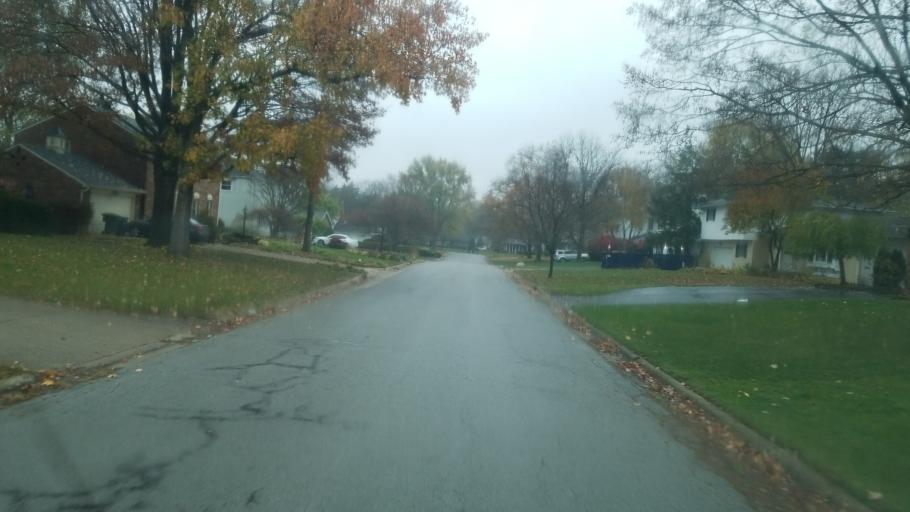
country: US
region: Ohio
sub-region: Franklin County
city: Worthington
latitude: 40.0506
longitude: -83.0408
